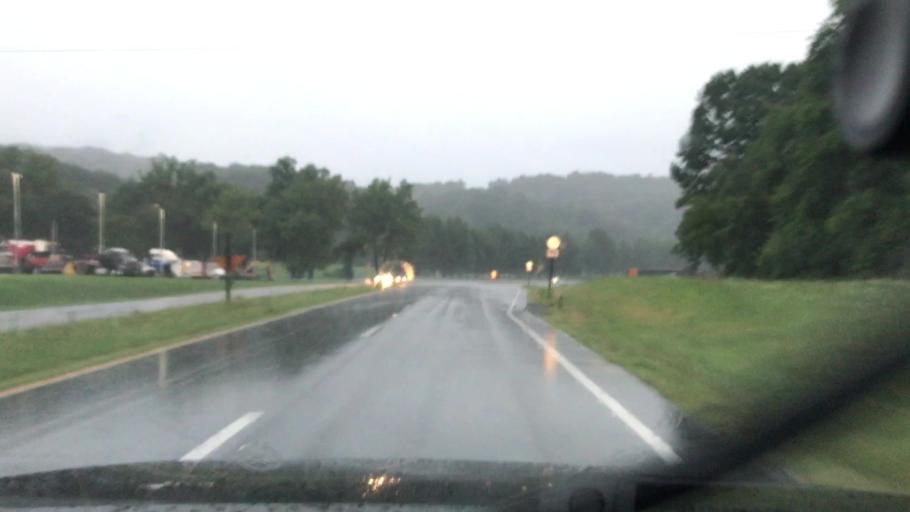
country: US
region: Virginia
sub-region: Giles County
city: Pearisburg
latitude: 37.3501
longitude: -80.7668
